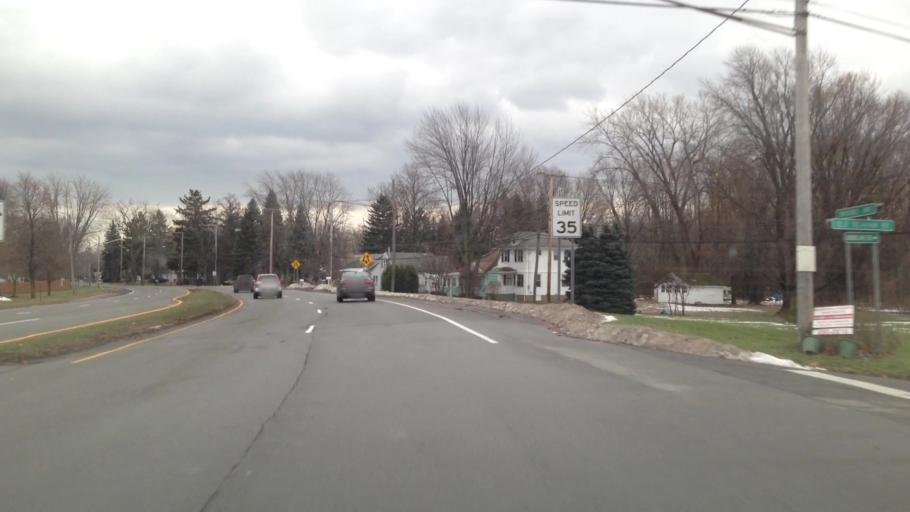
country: US
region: New York
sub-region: Monroe County
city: North Gates
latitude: 43.1310
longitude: -77.6859
